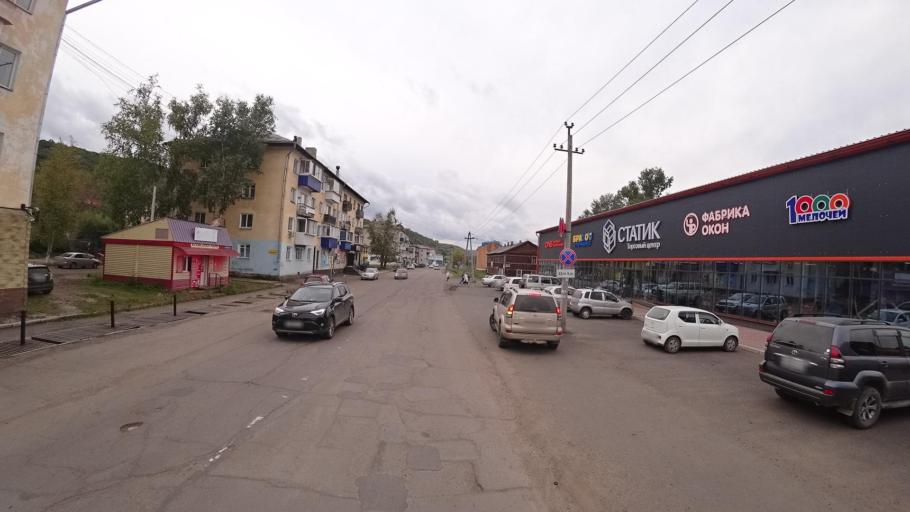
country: RU
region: Jewish Autonomous Oblast
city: Khingansk
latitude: 49.0110
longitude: 131.0571
